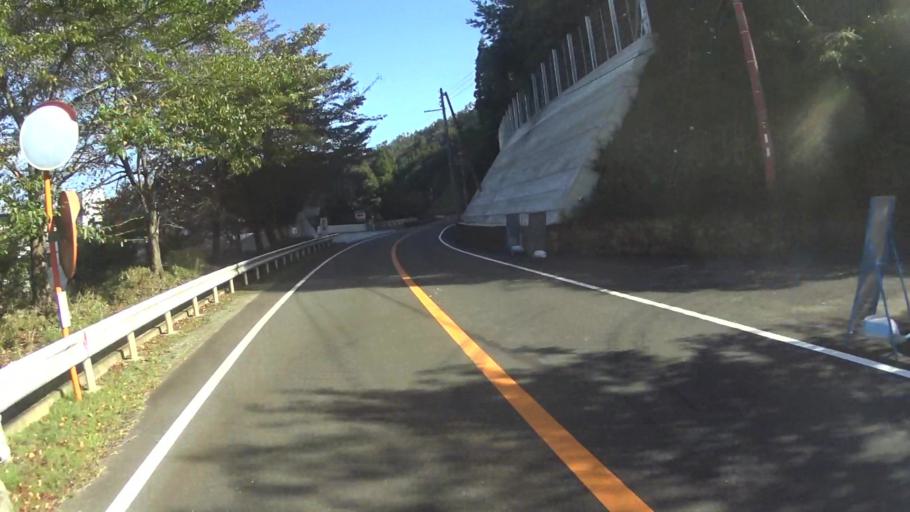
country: JP
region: Kyoto
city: Kameoka
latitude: 35.1450
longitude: 135.5178
